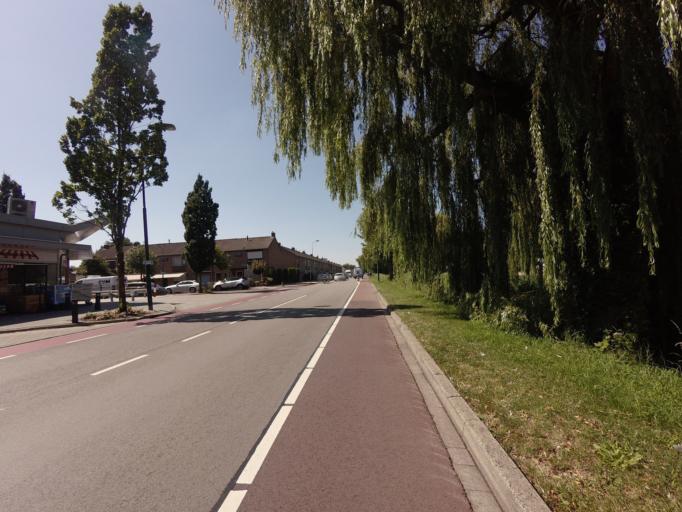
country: NL
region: Utrecht
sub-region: Stichtse Vecht
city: Maarssen
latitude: 52.1441
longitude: 5.0450
